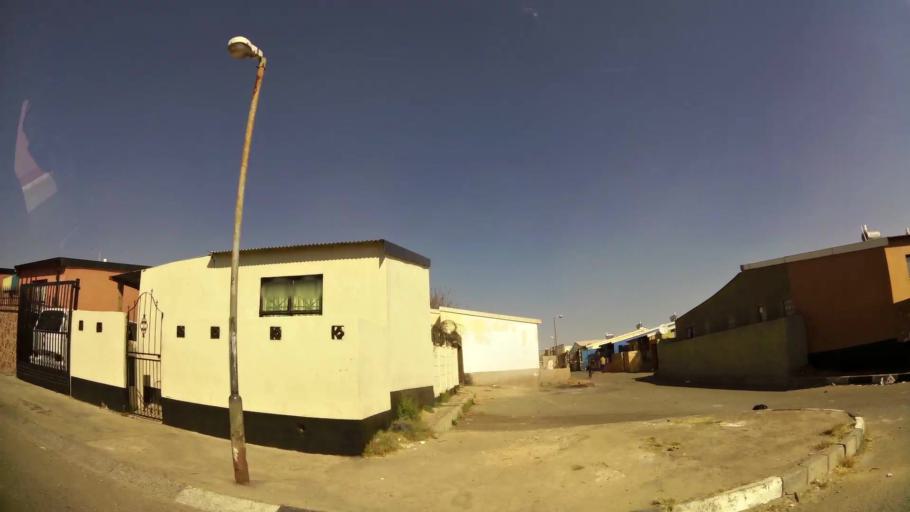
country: ZA
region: Gauteng
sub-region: City of Johannesburg Metropolitan Municipality
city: Johannesburg
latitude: -26.1846
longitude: 27.9775
